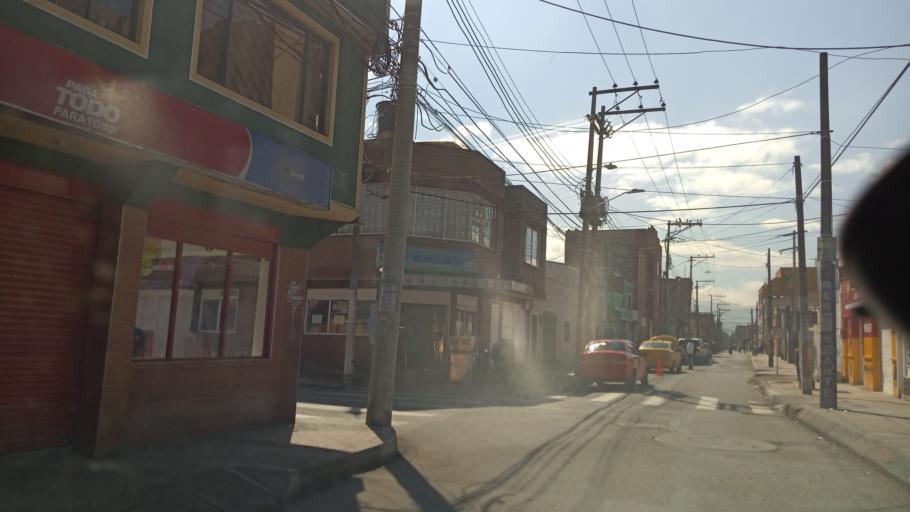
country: CO
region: Cundinamarca
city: Funza
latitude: 4.6736
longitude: -74.1482
